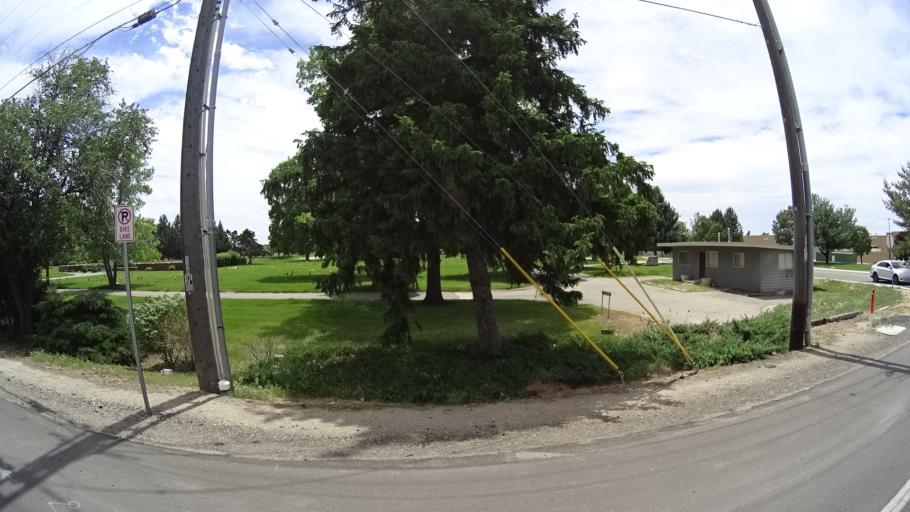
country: US
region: Idaho
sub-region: Ada County
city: Meridian
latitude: 43.6194
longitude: -116.3417
